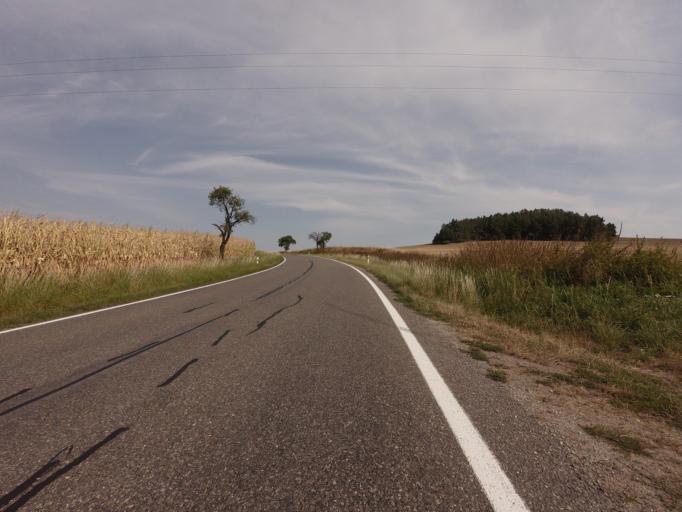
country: CZ
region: Central Bohemia
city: Petrovice
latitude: 49.5082
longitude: 14.3640
